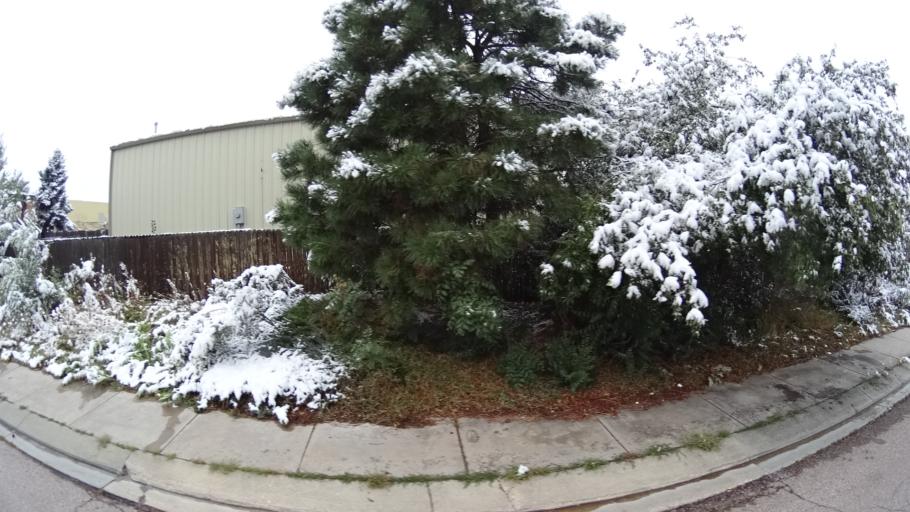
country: US
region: Colorado
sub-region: El Paso County
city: Colorado Springs
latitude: 38.9180
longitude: -104.7840
